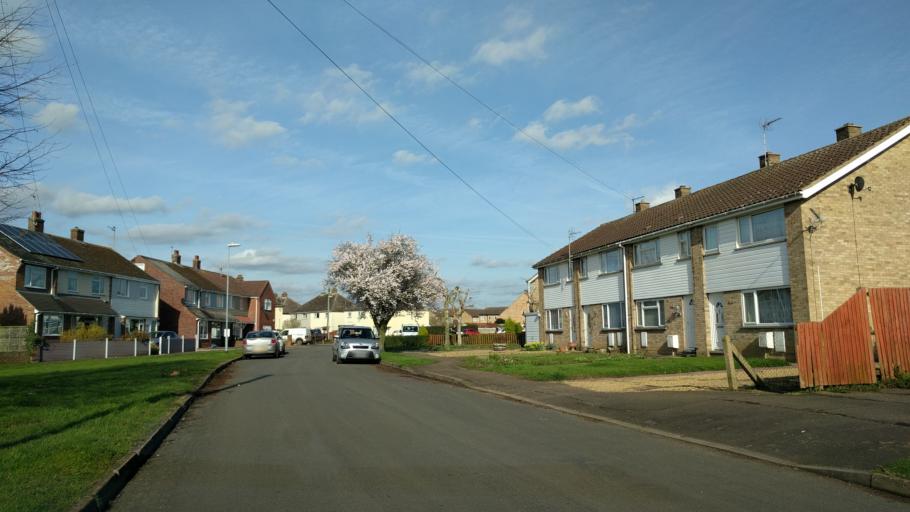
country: GB
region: England
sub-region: Cambridgeshire
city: Chatteris
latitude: 52.4475
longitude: 0.0415
